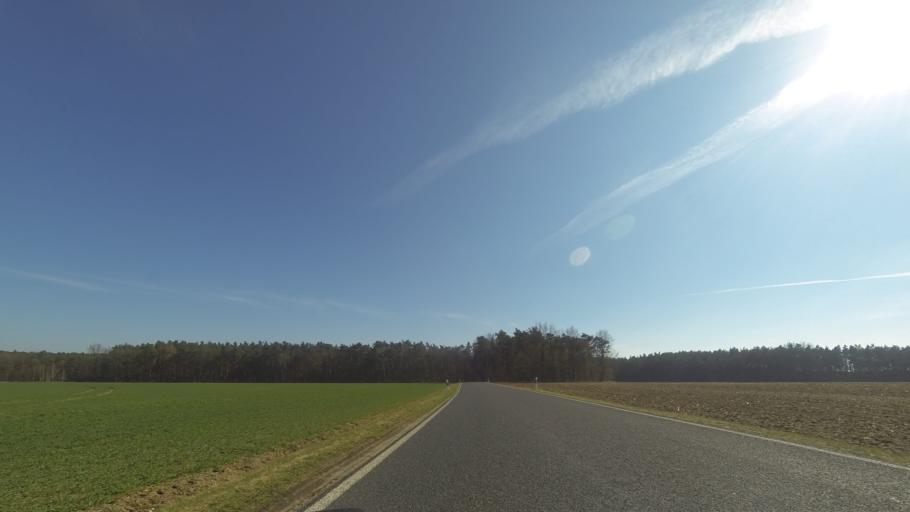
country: DE
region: Saxony
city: Tauscha
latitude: 51.2324
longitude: 13.7998
